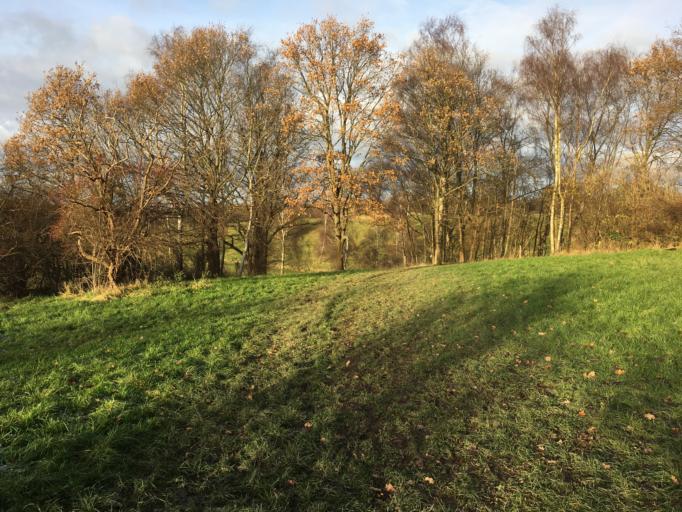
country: DK
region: Capital Region
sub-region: Fureso Kommune
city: Farum
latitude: 55.7909
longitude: 12.3428
